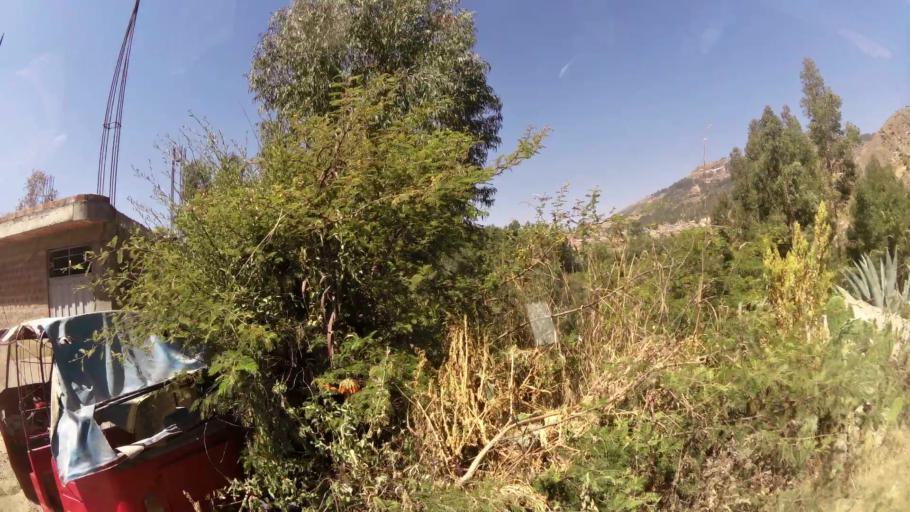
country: PE
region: Ayacucho
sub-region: Provincia de Huamanga
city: Carmen Alto
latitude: -13.1787
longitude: -74.2300
